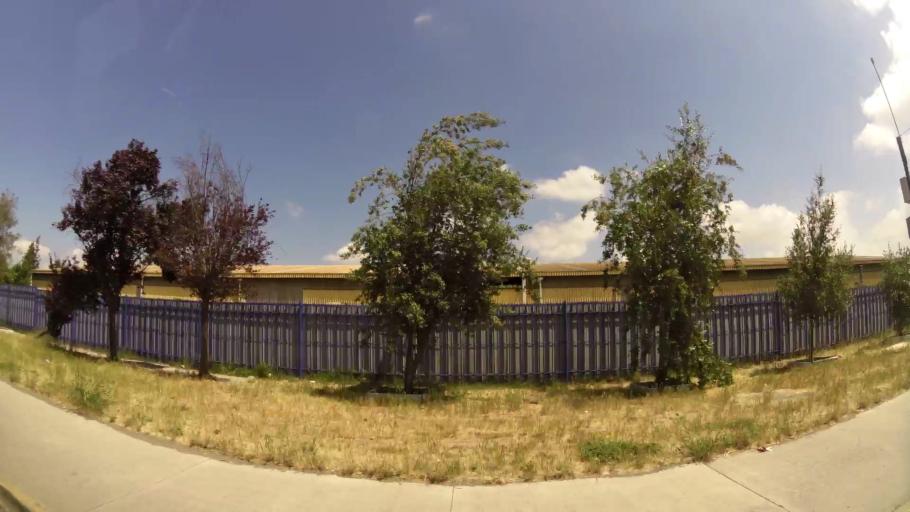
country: CL
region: Santiago Metropolitan
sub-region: Provincia de Maipo
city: San Bernardo
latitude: -33.5230
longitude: -70.7258
